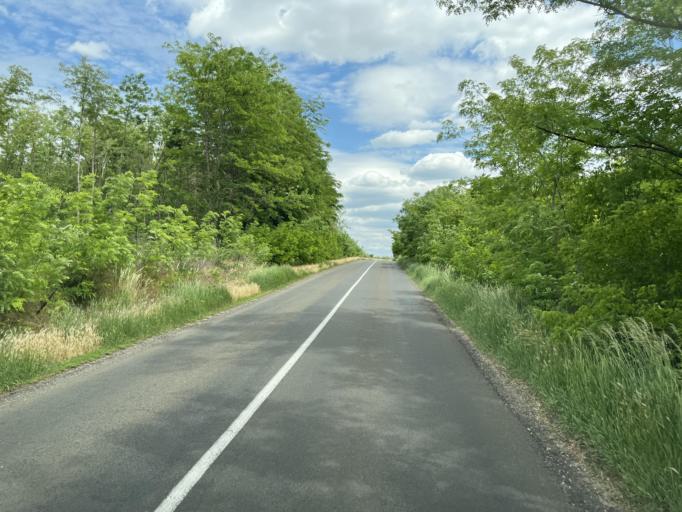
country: HU
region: Pest
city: Tapioszecso
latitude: 47.4733
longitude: 19.6232
